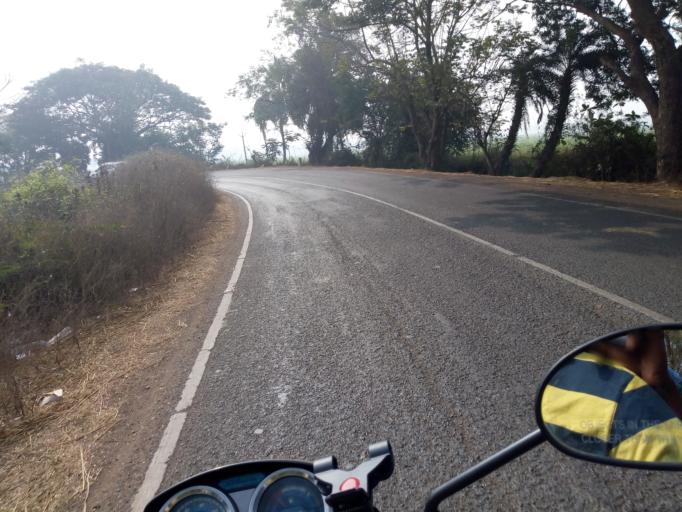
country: IN
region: Andhra Pradesh
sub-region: West Godavari
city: Tadepallegudem
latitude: 16.8010
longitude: 81.4115
